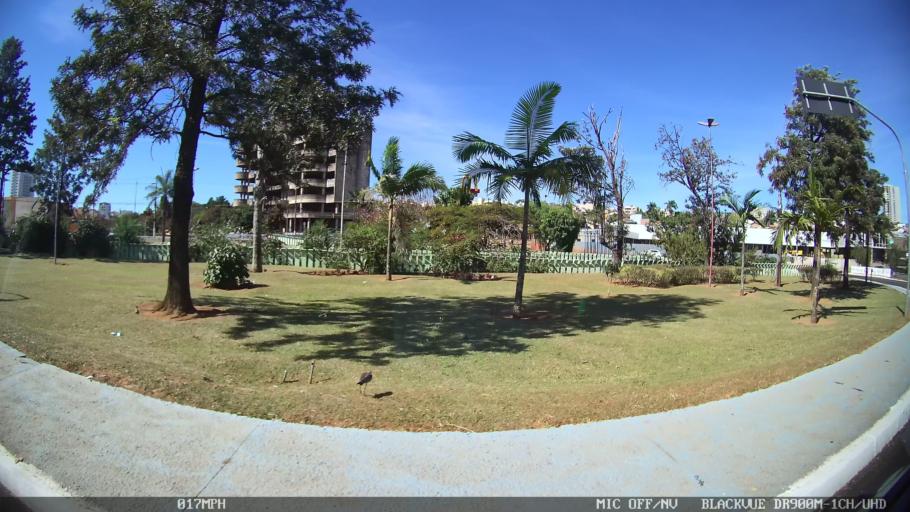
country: BR
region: Sao Paulo
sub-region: Franca
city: Franca
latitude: -20.5522
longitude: -47.4048
